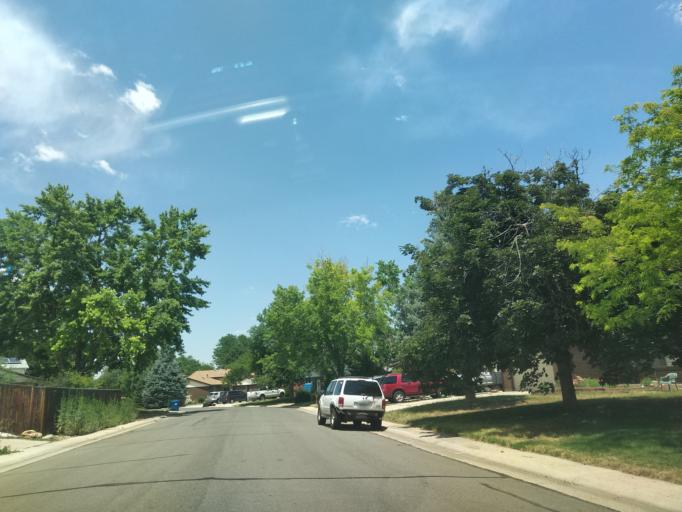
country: US
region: Colorado
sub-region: Jefferson County
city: Lakewood
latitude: 39.6798
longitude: -105.0918
